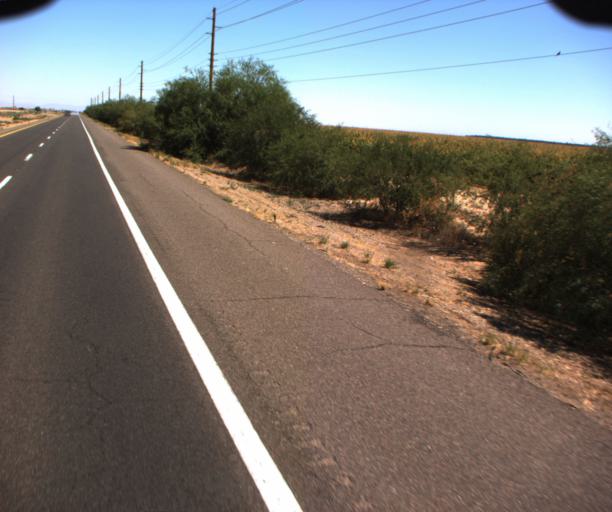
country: US
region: Arizona
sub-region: Pinal County
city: Maricopa
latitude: 32.9786
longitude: -112.0477
